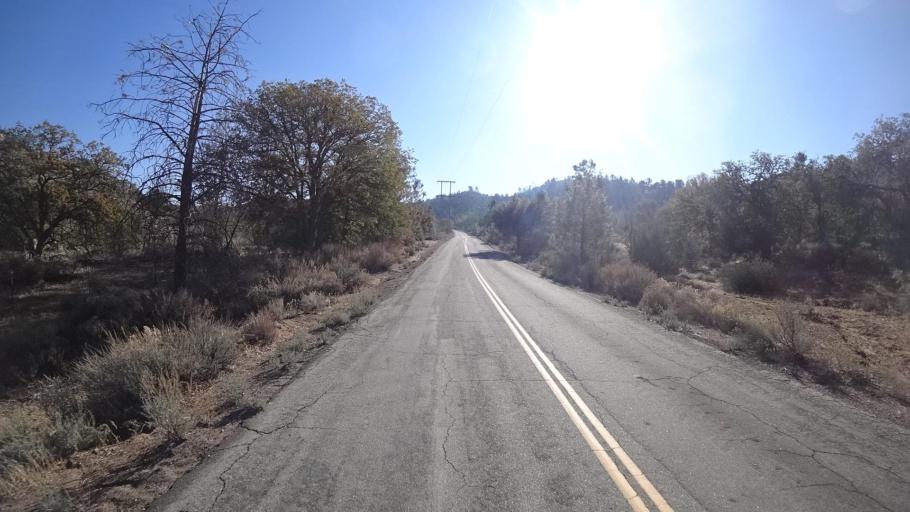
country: US
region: California
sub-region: Kern County
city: Bodfish
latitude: 35.3871
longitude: -118.4240
